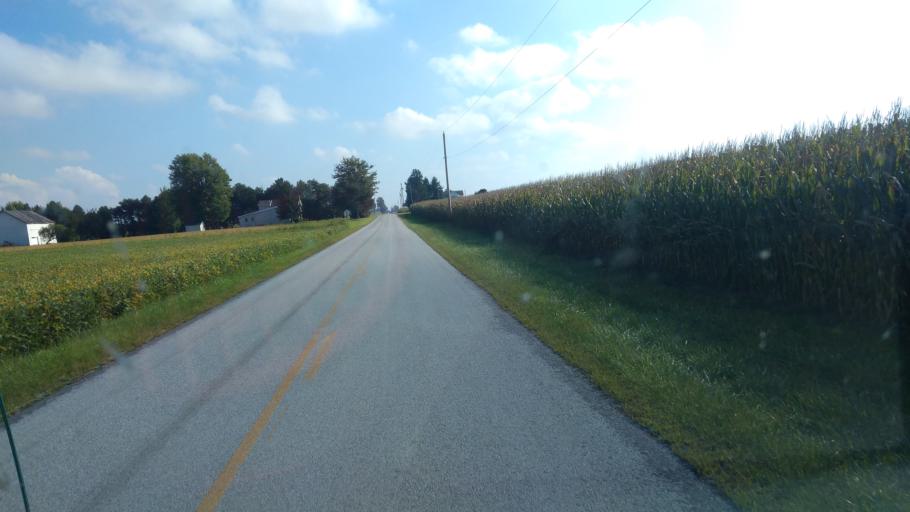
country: US
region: Ohio
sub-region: Hardin County
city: Forest
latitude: 40.7570
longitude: -83.5158
